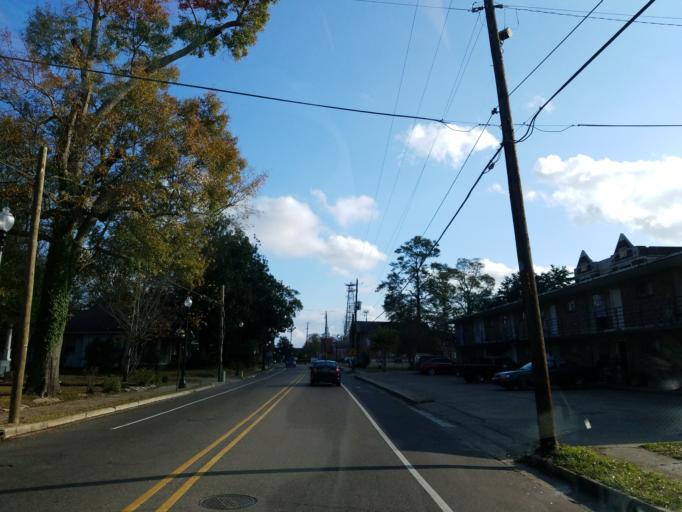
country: US
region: Mississippi
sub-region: Forrest County
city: Hattiesburg
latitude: 31.3305
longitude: -89.2955
